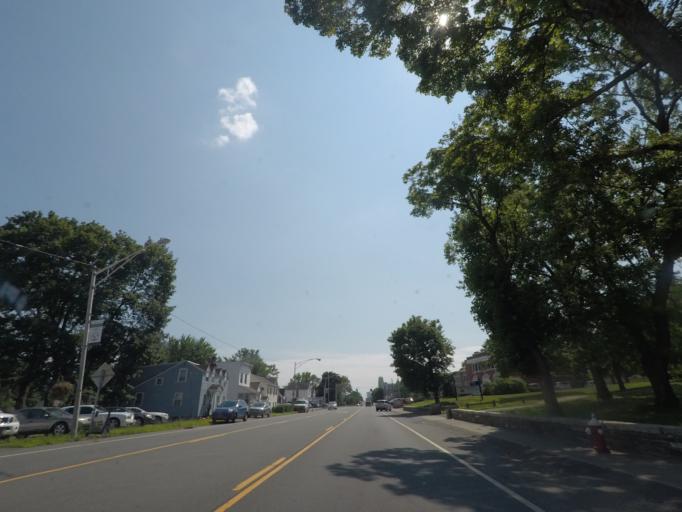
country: US
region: New York
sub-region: Albany County
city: Menands
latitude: 42.6930
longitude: -73.7238
